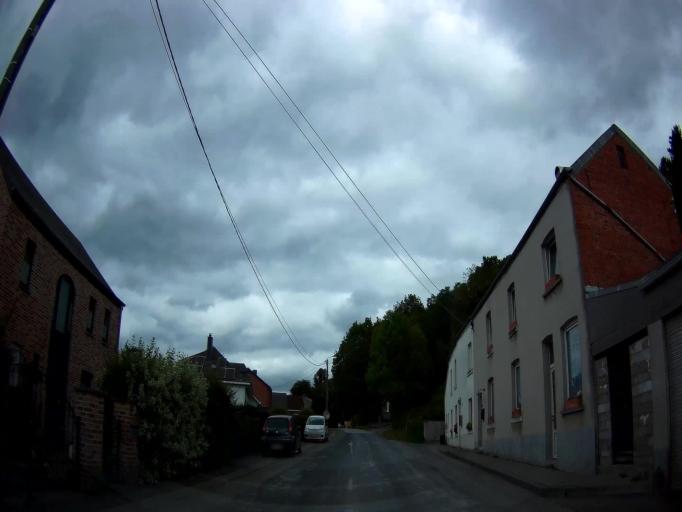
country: BE
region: Wallonia
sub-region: Province de Namur
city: Rochefort
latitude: 50.1639
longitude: 5.2264
